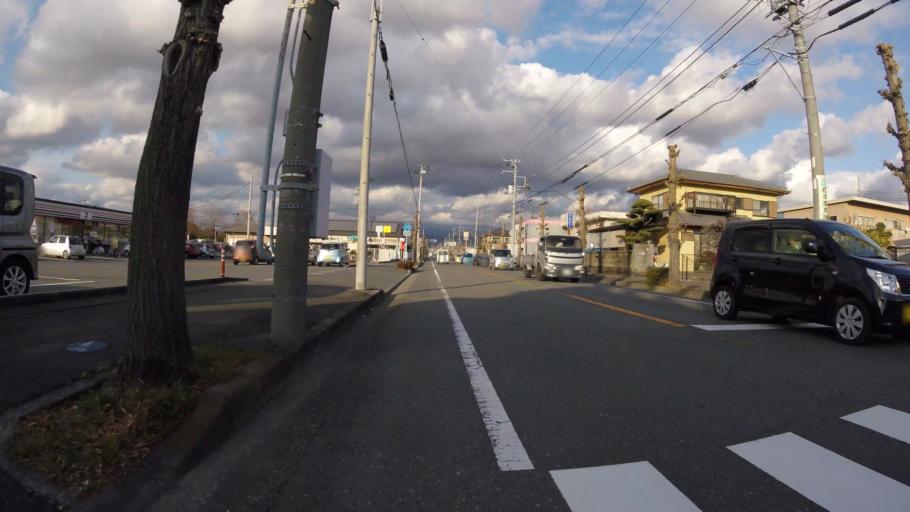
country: JP
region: Shizuoka
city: Fuji
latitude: 35.1533
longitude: 138.6830
